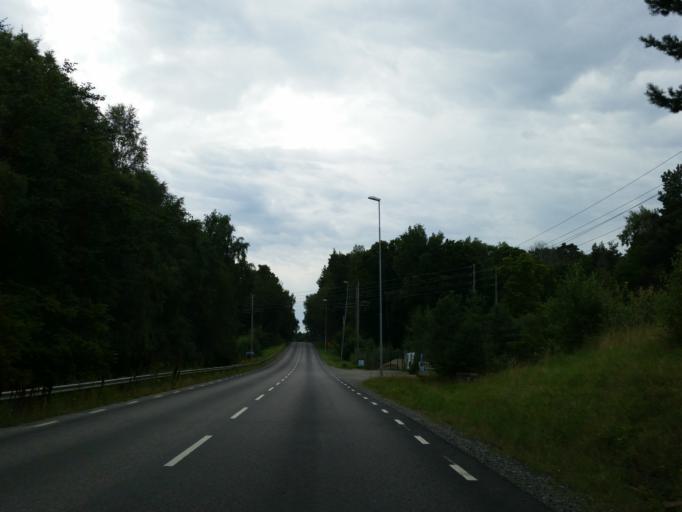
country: SE
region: Stockholm
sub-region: Botkyrka Kommun
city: Eriksberg
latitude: 59.2405
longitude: 17.7831
